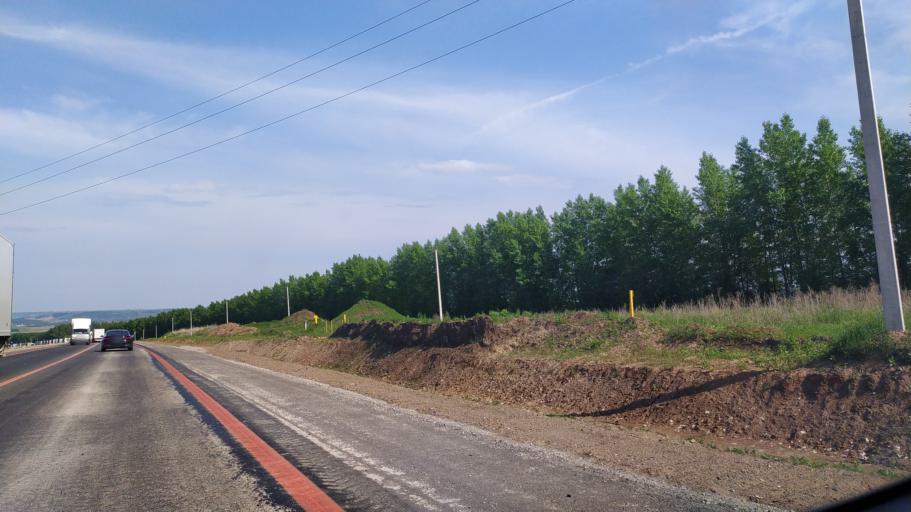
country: RU
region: Tatarstan
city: Nizhniye Vyazovyye
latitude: 55.7235
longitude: 48.4435
